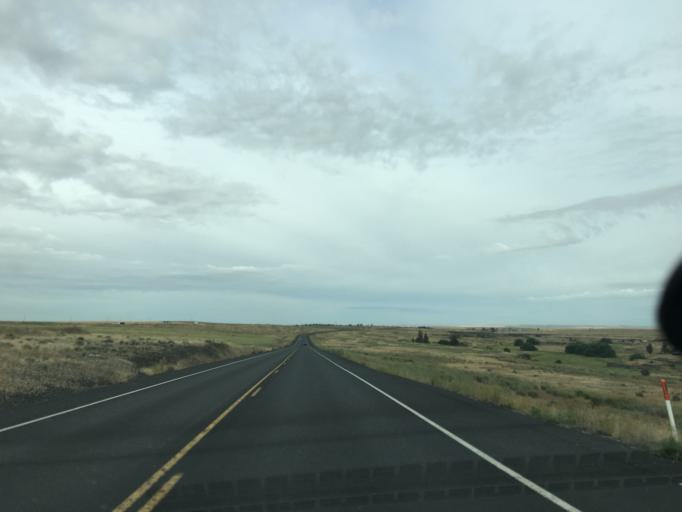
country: US
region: Washington
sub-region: Okanogan County
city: Coulee Dam
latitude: 47.7576
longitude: -118.6502
